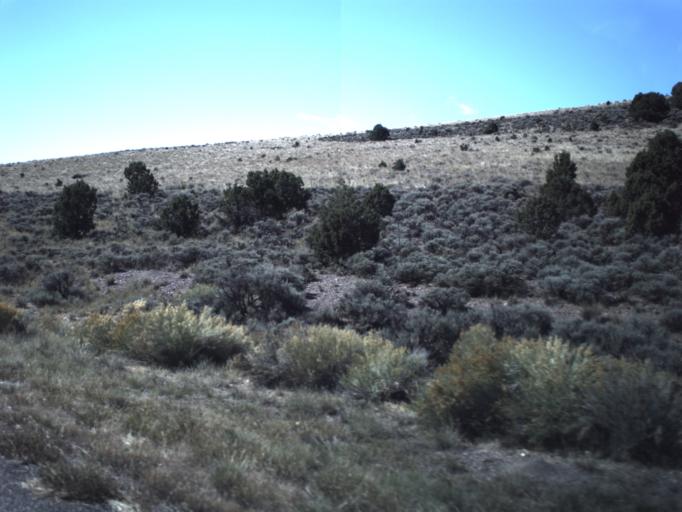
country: US
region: Utah
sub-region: Sevier County
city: Monroe
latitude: 38.5416
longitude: -111.8724
